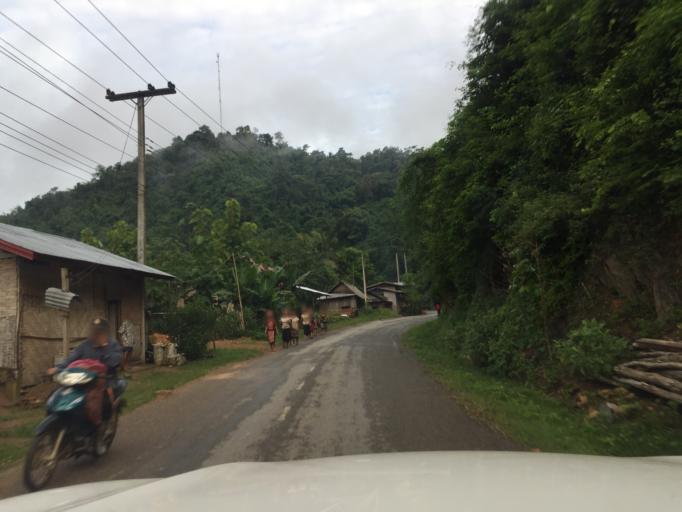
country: LA
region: Phongsali
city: Khoa
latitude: 21.1026
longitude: 102.2587
